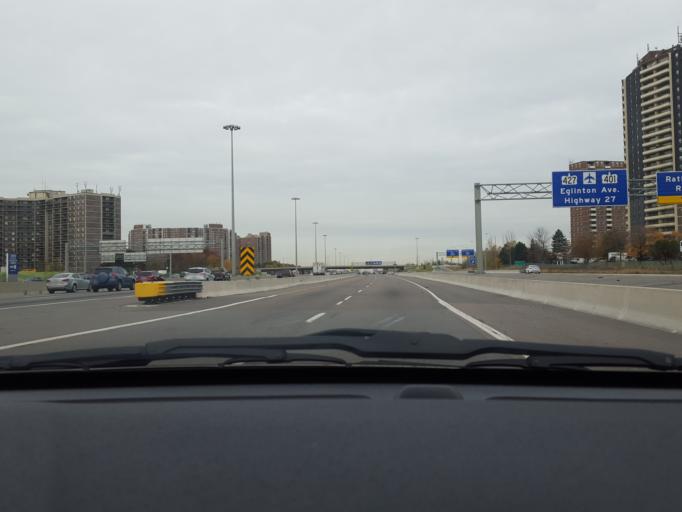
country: CA
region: Ontario
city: Etobicoke
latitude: 43.6496
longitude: -79.5648
